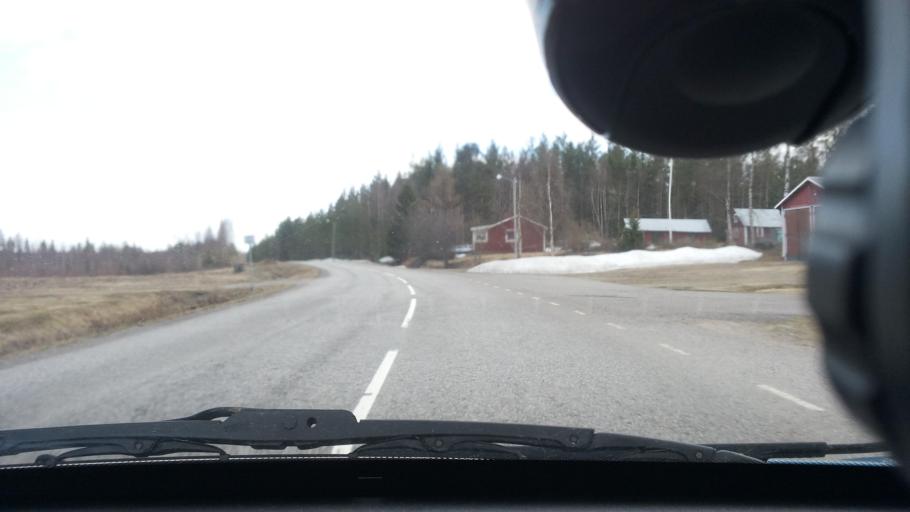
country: SE
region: Norrbotten
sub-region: Lulea Kommun
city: Sodra Sunderbyn
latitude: 65.6610
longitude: 21.8279
